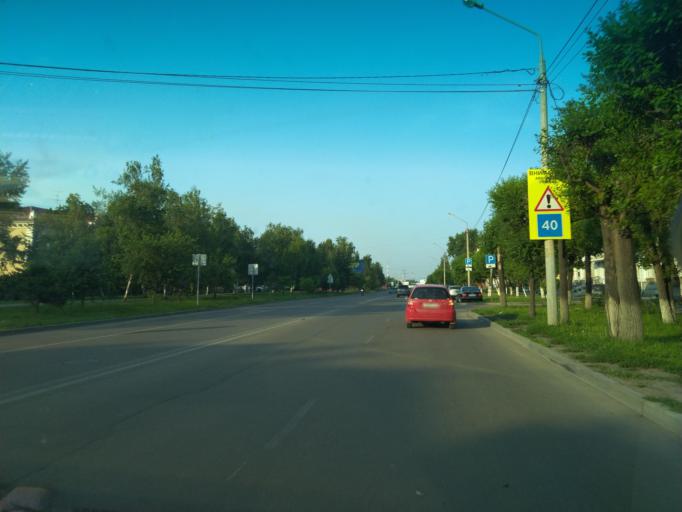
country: RU
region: Krasnoyarskiy
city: Krasnoyarsk
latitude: 56.0004
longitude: 92.9416
